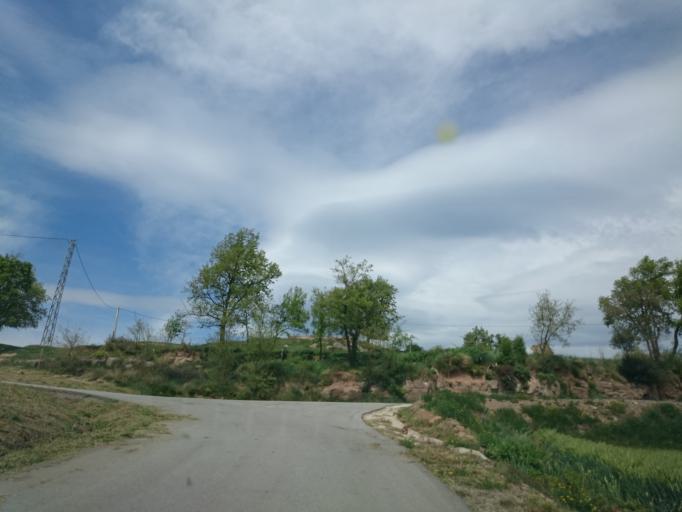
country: ES
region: Catalonia
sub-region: Provincia de Barcelona
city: Prats de Llucanes
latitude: 42.0083
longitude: 2.0483
